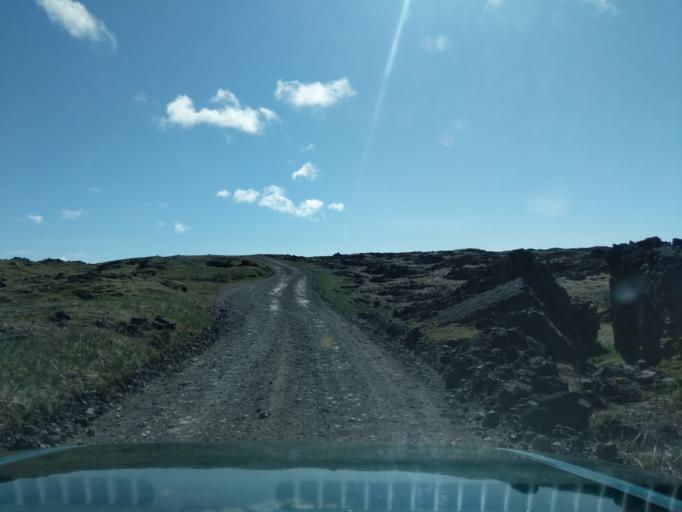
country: IS
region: West
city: Olafsvik
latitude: 64.8792
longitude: -23.9900
